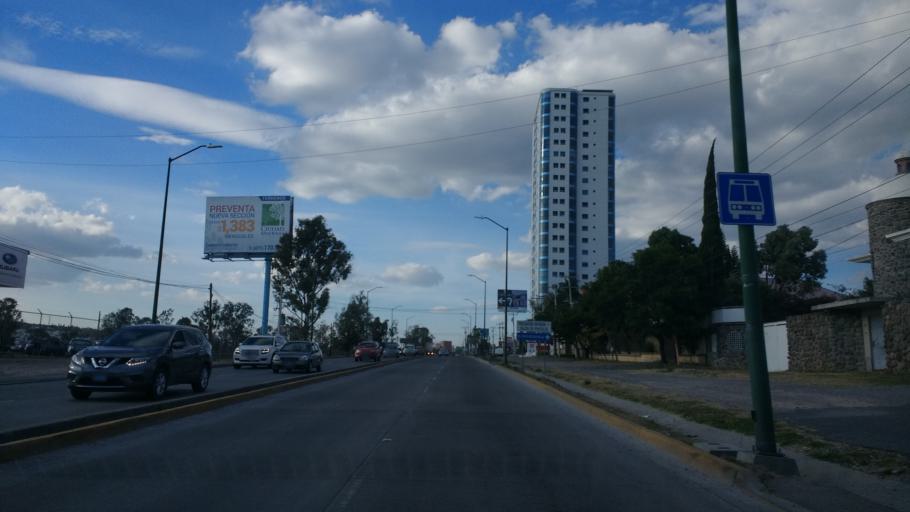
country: MX
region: Guanajuato
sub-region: Leon
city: La Ermita
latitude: 21.1574
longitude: -101.7217
